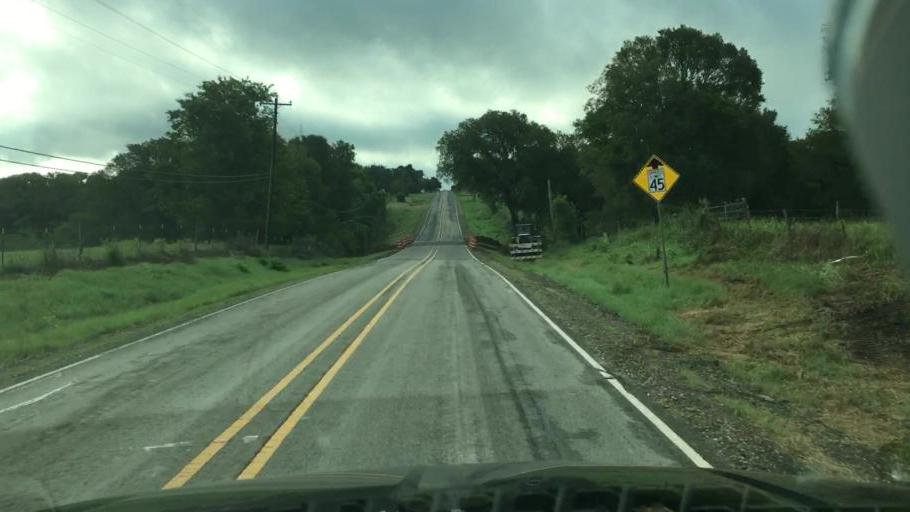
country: US
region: Texas
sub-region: Lee County
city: Lexington
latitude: 30.3660
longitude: -96.8360
